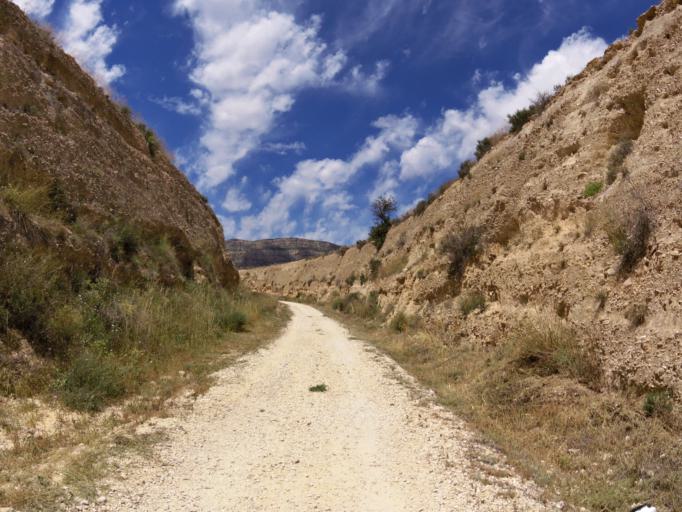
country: ES
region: Valencia
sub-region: Provincia de Alicante
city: Agost
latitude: 38.4513
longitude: -0.6688
